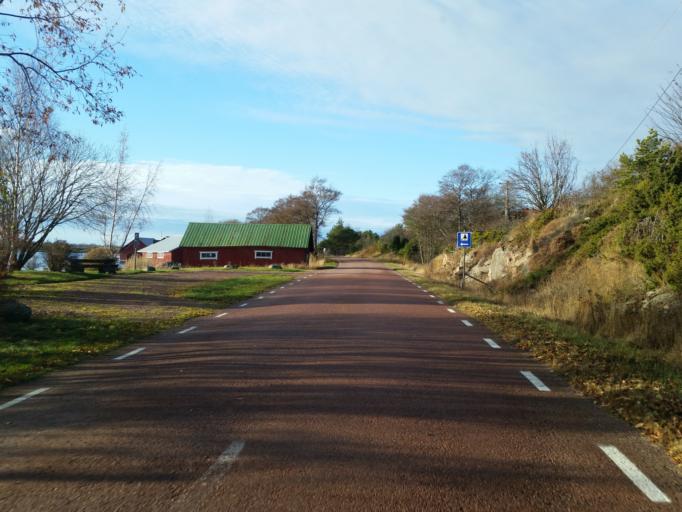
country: AX
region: Alands skaergard
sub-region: Kumlinge
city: Kumlinge
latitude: 60.2563
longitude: 20.7469
